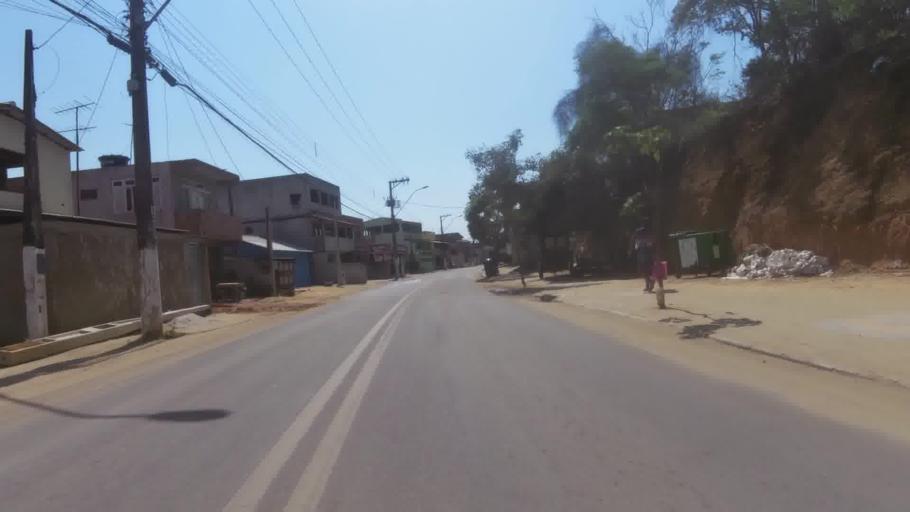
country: BR
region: Espirito Santo
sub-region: Itapemirim
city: Itapemirim
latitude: -21.0142
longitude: -40.8363
